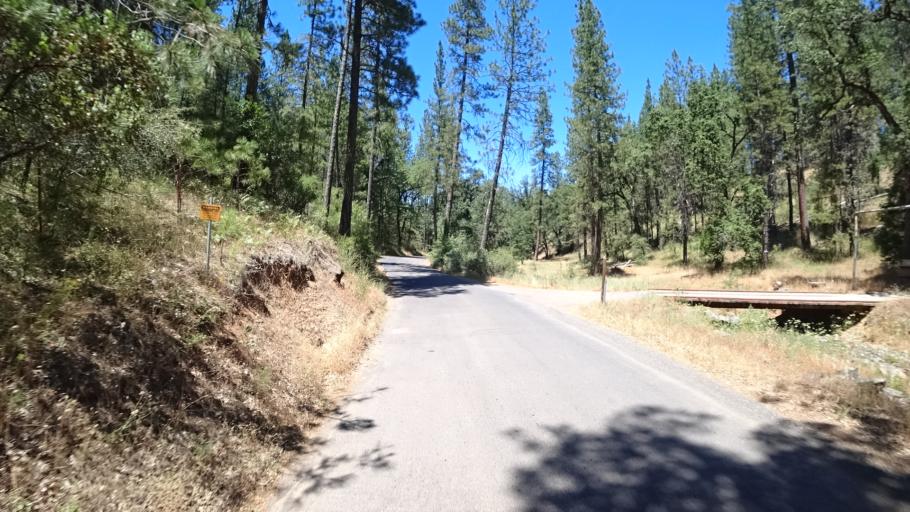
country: US
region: California
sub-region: Calaveras County
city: Mountain Ranch
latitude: 38.2681
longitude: -120.4914
